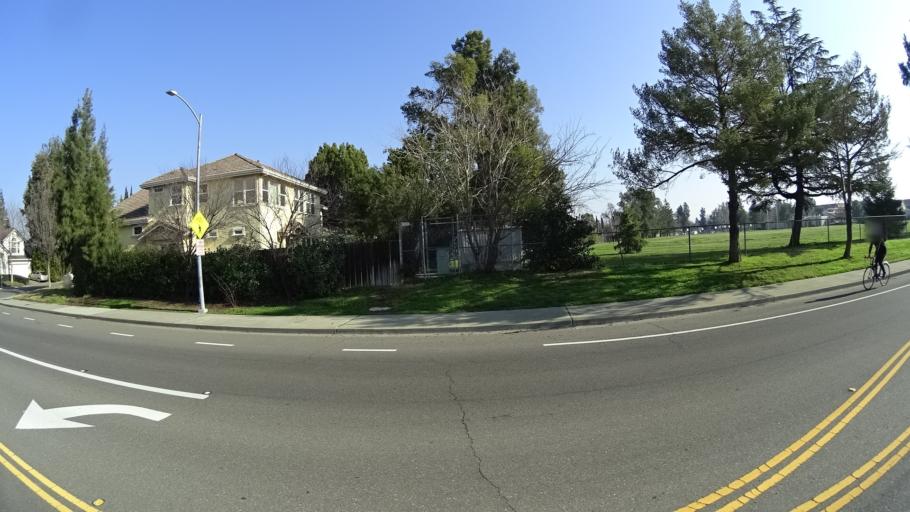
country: US
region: California
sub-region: Yolo County
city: Davis
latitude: 38.5526
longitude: -121.7801
